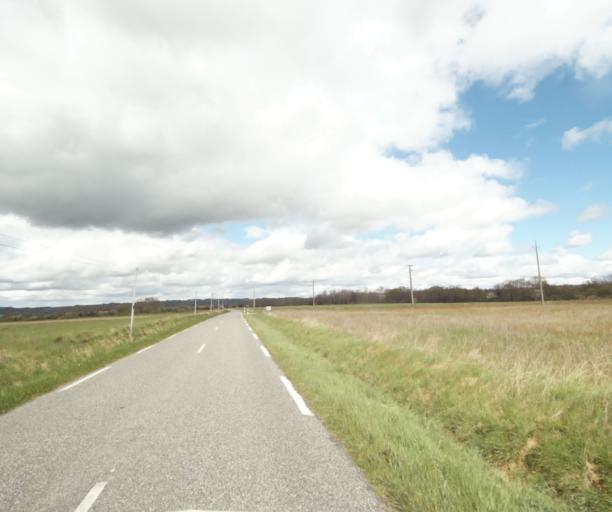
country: FR
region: Midi-Pyrenees
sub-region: Departement de la Haute-Garonne
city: Calmont
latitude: 43.2521
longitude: 1.6369
